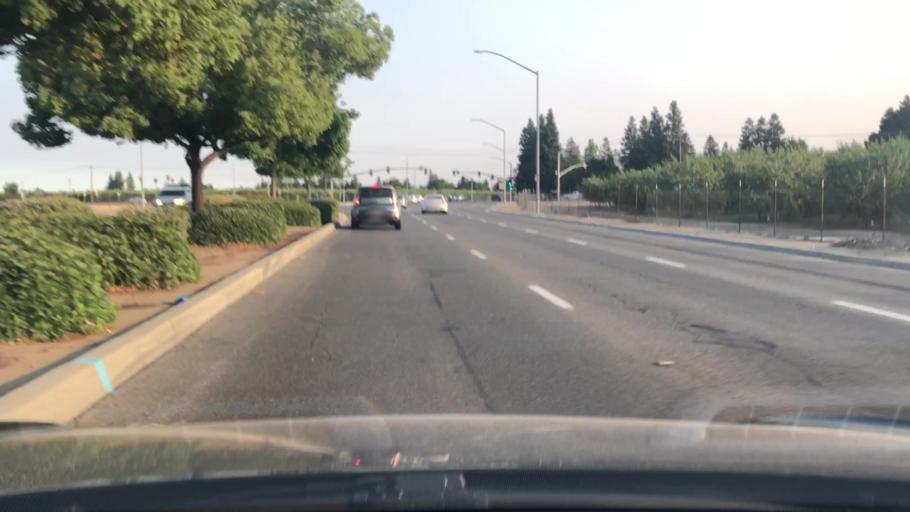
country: US
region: California
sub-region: Fresno County
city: Clovis
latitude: 36.8216
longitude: -119.7281
